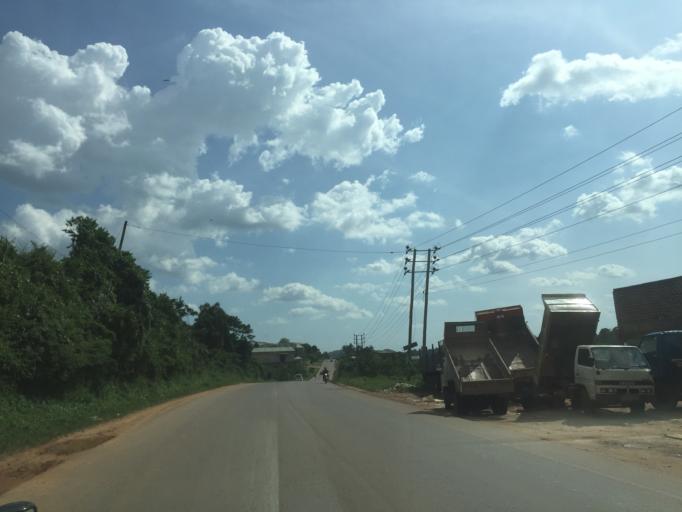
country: UG
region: Central Region
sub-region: Wakiso District
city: Wakiso
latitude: 0.4874
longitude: 32.5220
